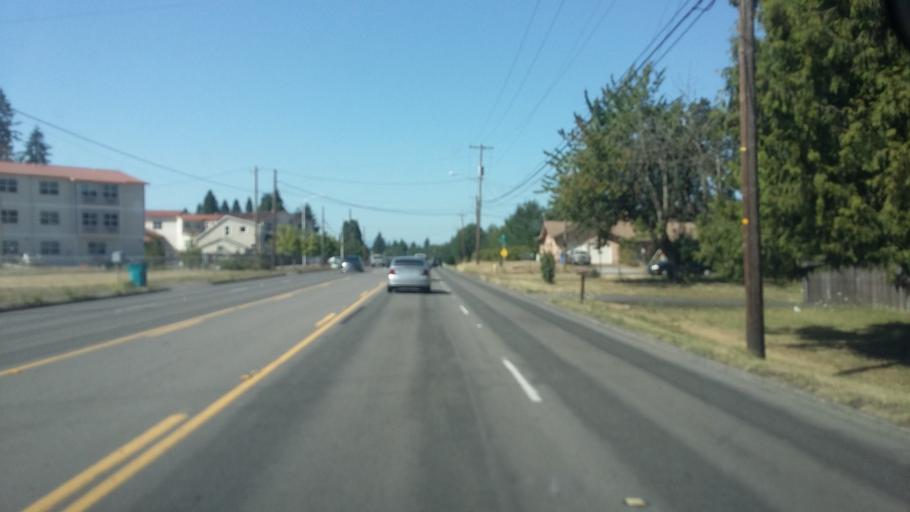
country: US
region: Washington
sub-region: Clark County
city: Orchards
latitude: 45.6385
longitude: -122.5579
